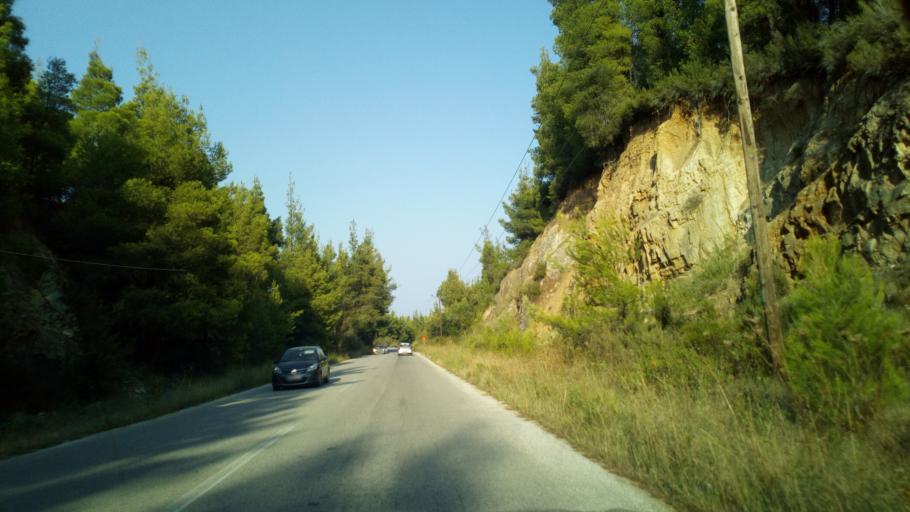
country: GR
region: Central Macedonia
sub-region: Nomos Chalkidikis
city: Neos Marmaras
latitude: 40.1794
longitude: 23.8218
